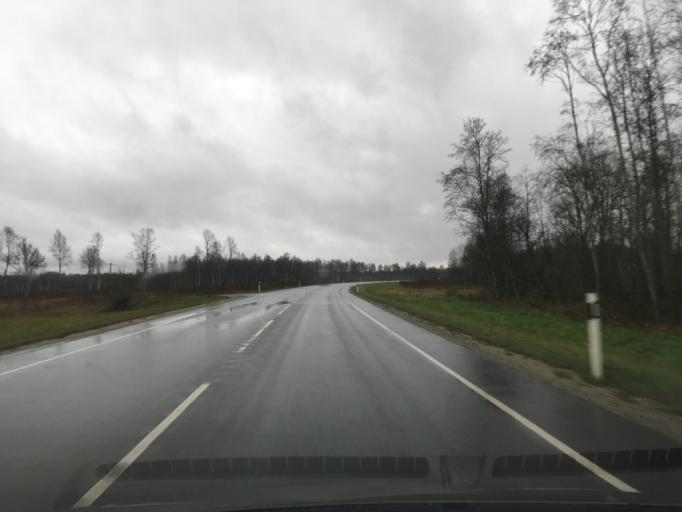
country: EE
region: Laeaene
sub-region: Lihula vald
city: Lihula
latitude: 58.7990
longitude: 24.0466
